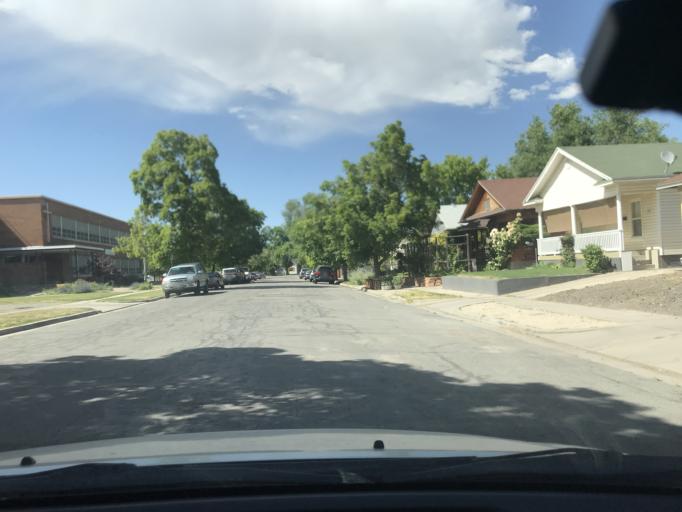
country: US
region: Utah
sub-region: Salt Lake County
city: Salt Lake City
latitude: 40.7611
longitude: -111.9209
